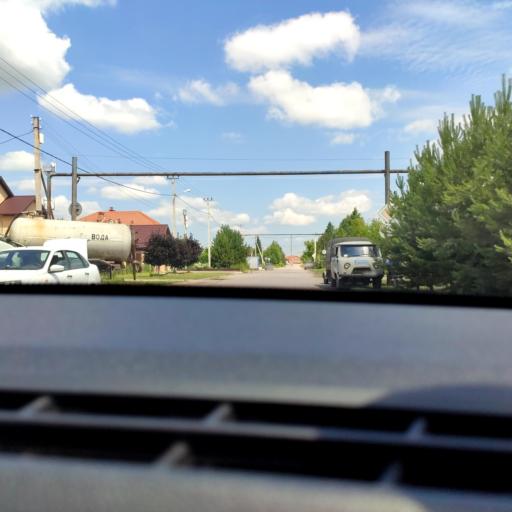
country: RU
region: Samara
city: Podstepki
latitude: 53.5698
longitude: 49.0799
